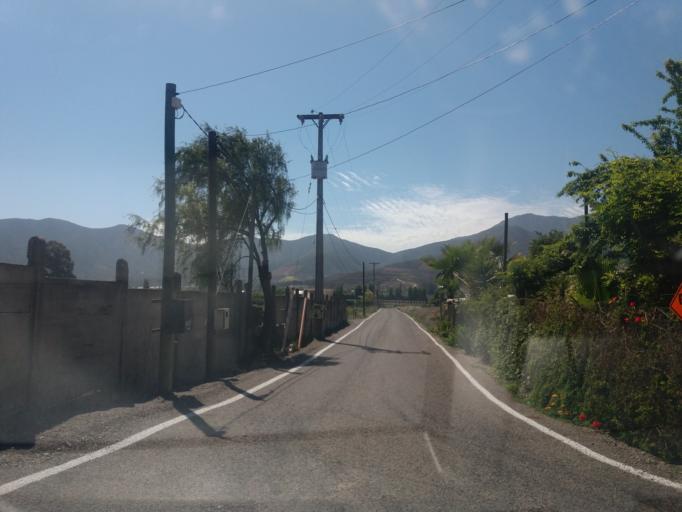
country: CL
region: Valparaiso
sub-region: Provincia de Quillota
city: Quillota
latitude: -32.8571
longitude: -71.2091
